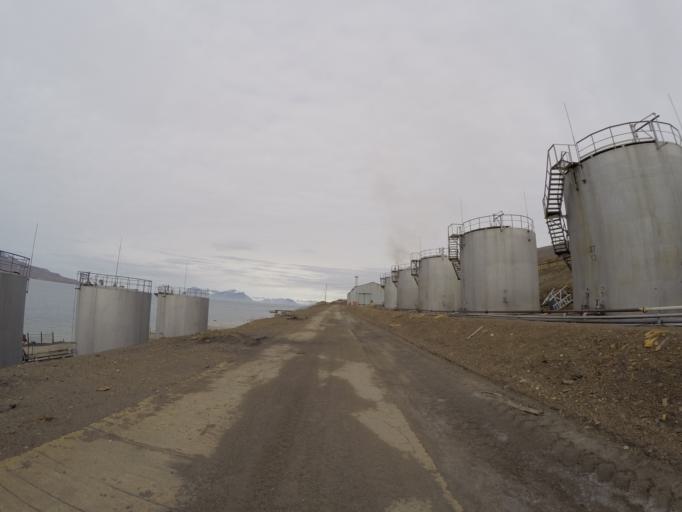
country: SJ
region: Svalbard
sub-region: Spitsbergen
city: Longyearbyen
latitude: 78.0516
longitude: 14.2129
